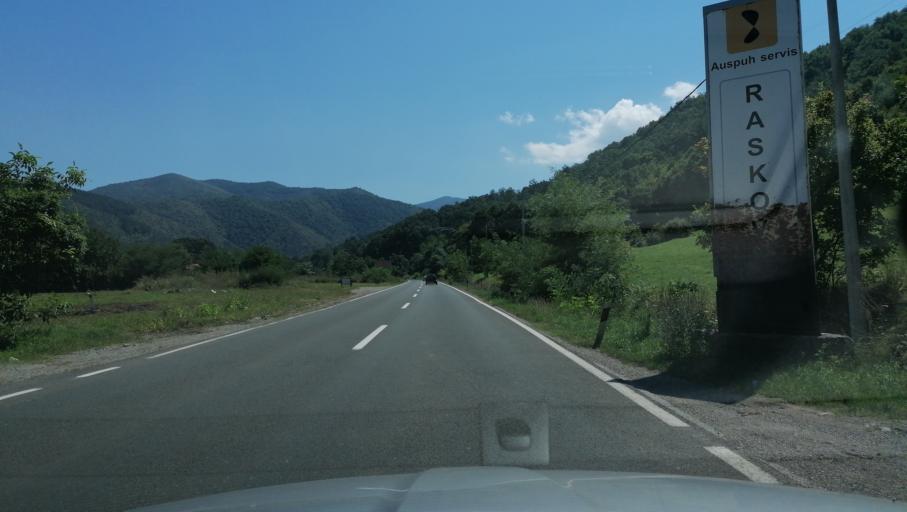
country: RS
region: Central Serbia
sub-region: Raski Okrug
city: Kraljevo
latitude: 43.6706
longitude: 20.5786
